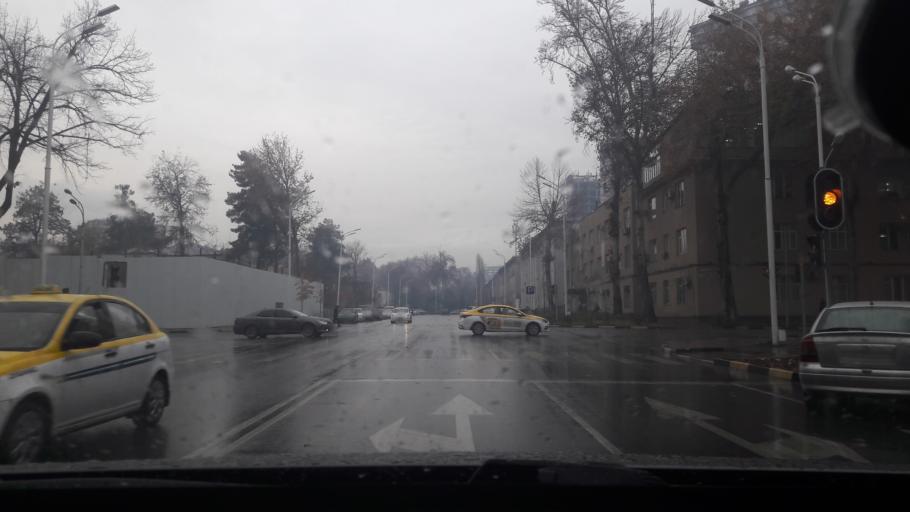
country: TJ
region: Dushanbe
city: Dushanbe
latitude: 38.5700
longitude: 68.7938
